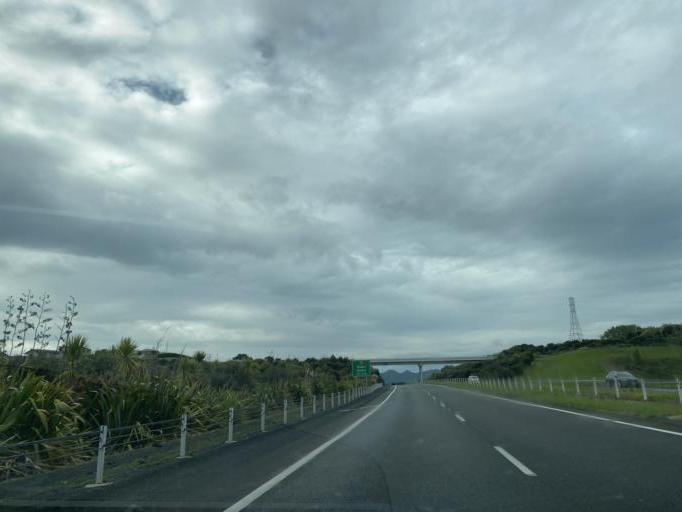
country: NZ
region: Waikato
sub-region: Waikato District
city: Ngaruawahia
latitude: -37.6353
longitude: 175.2067
